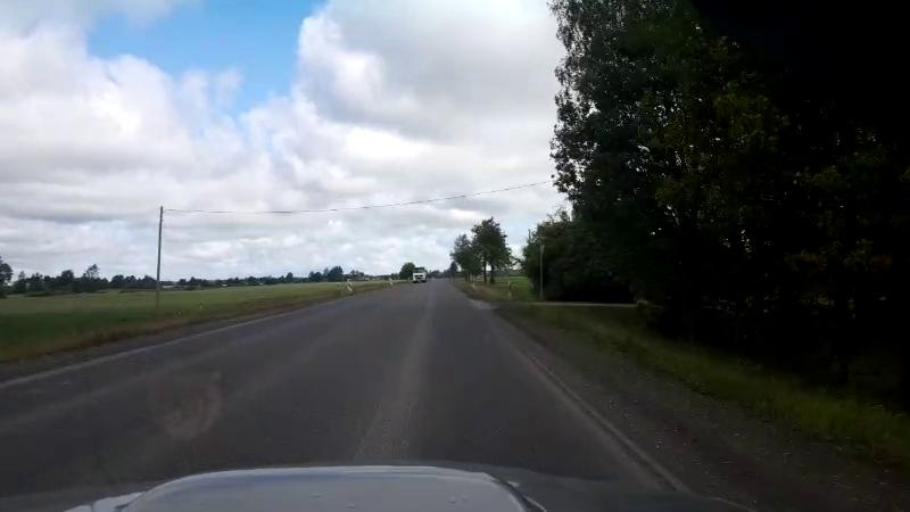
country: LV
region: Bauskas Rajons
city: Bauska
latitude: 56.3005
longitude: 24.3436
